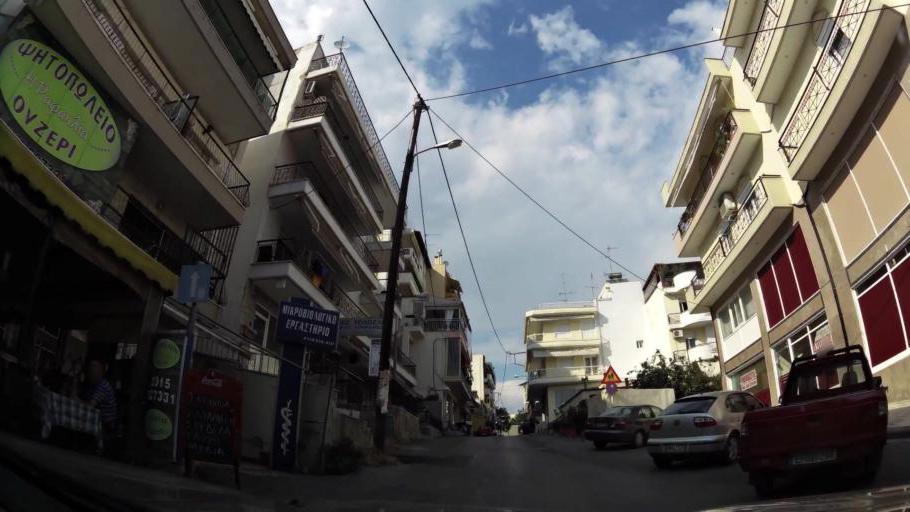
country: GR
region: Central Macedonia
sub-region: Nomos Thessalonikis
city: Sykies
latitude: 40.6583
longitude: 22.9569
